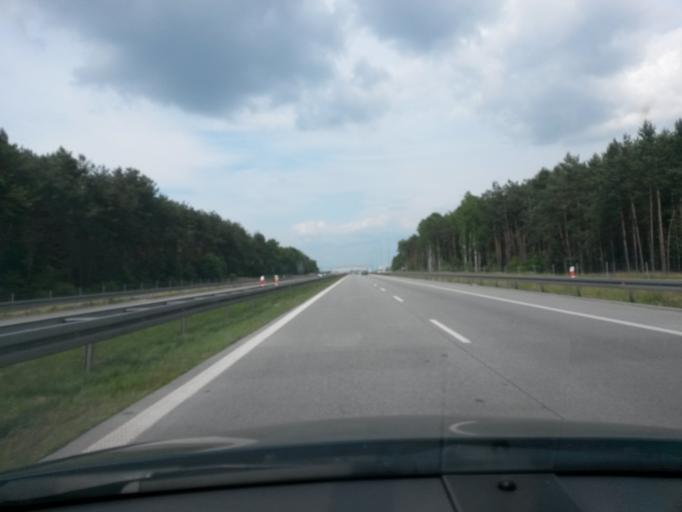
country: PL
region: Lodz Voivodeship
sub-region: Powiat tomaszowski
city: Czerniewice
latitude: 51.6396
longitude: 20.1243
